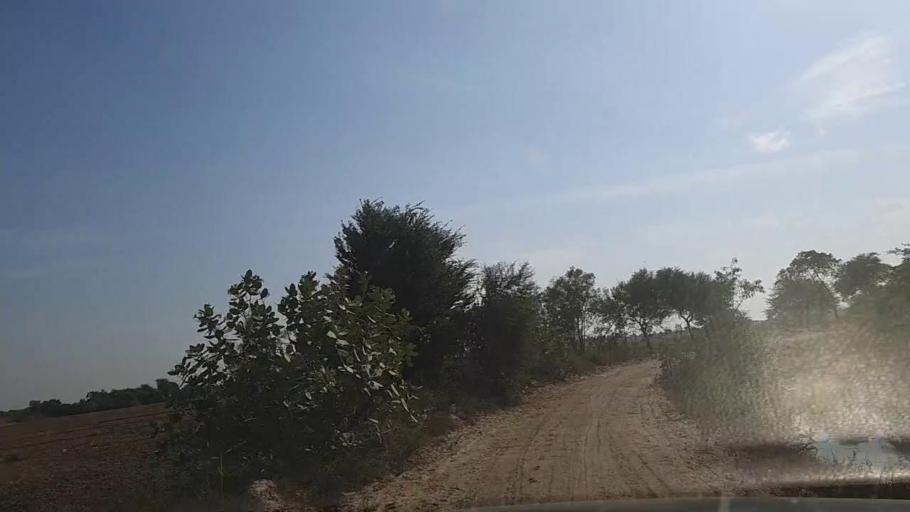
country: PK
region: Sindh
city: Bulri
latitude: 24.8466
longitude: 68.2906
